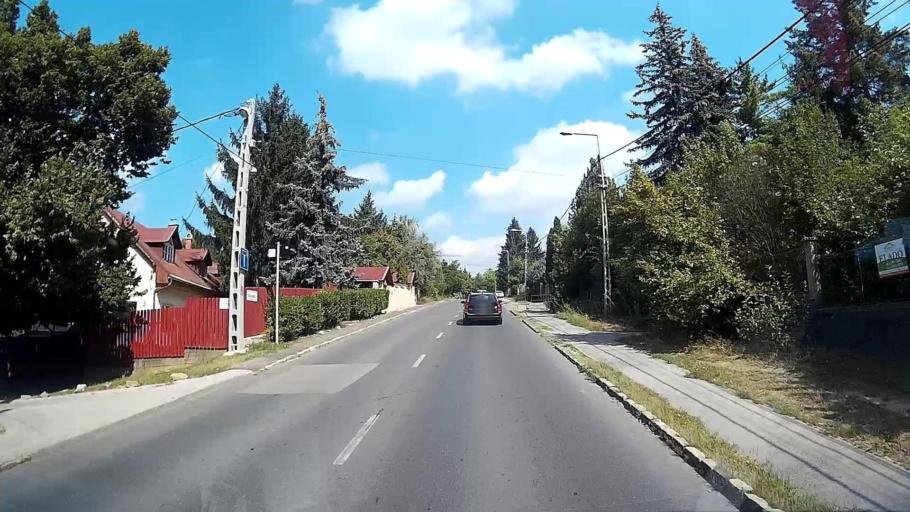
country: HU
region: Pest
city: Solymar
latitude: 47.5551
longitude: 18.9488
